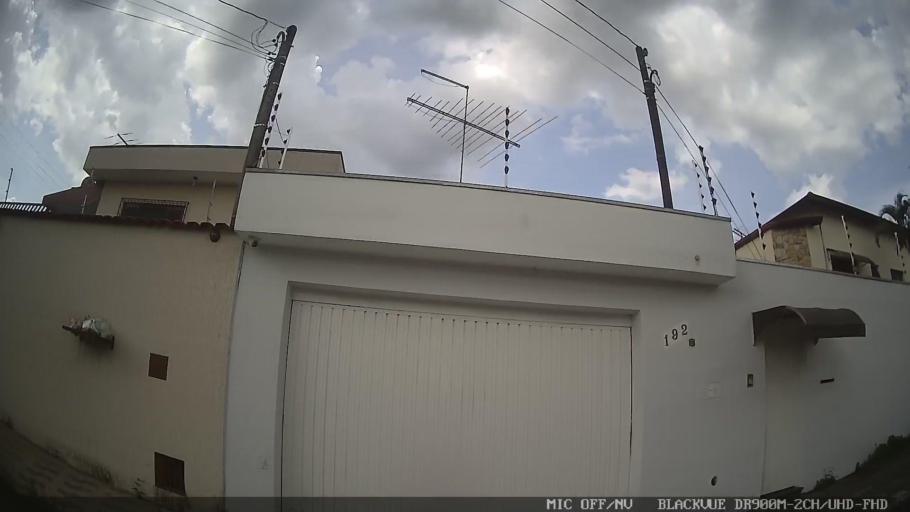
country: BR
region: Sao Paulo
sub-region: Suzano
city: Suzano
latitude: -23.5390
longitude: -46.3168
